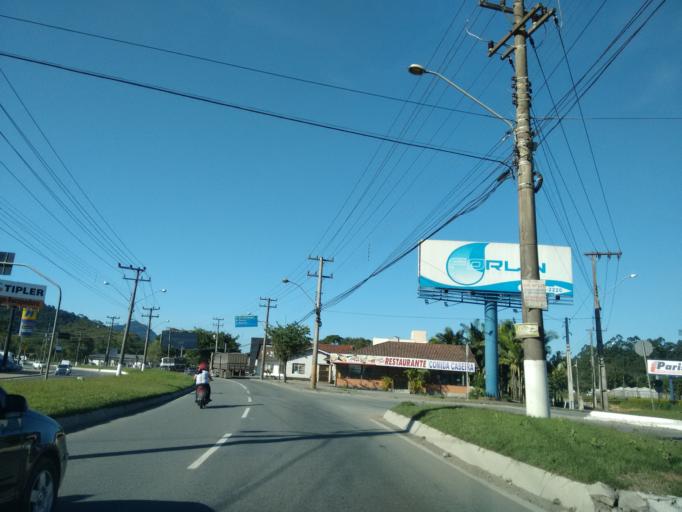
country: BR
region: Santa Catarina
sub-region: Guaramirim
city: Guaramirim
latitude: -26.4788
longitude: -49.0342
